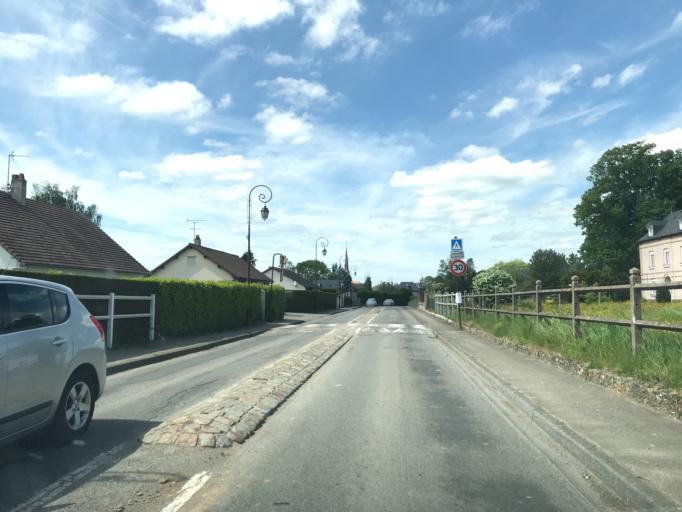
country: FR
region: Haute-Normandie
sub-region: Departement de l'Eure
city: Nassandres
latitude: 49.1646
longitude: 0.7892
